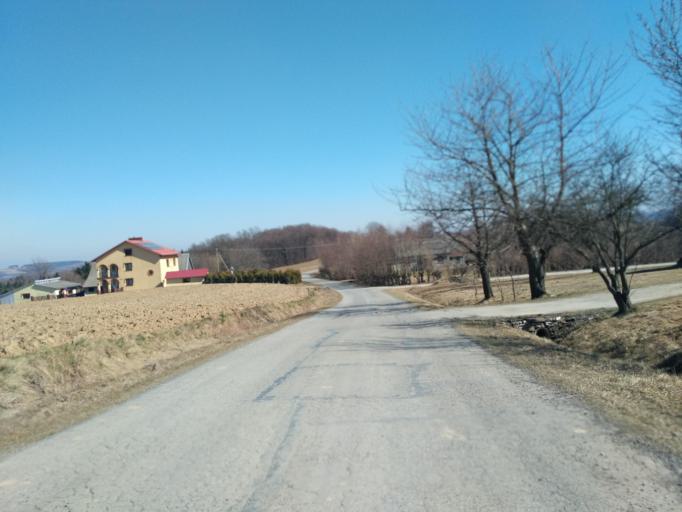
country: PL
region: Subcarpathian Voivodeship
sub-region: Powiat ropczycko-sedziszowski
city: Niedzwiada
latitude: 49.9519
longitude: 21.5128
